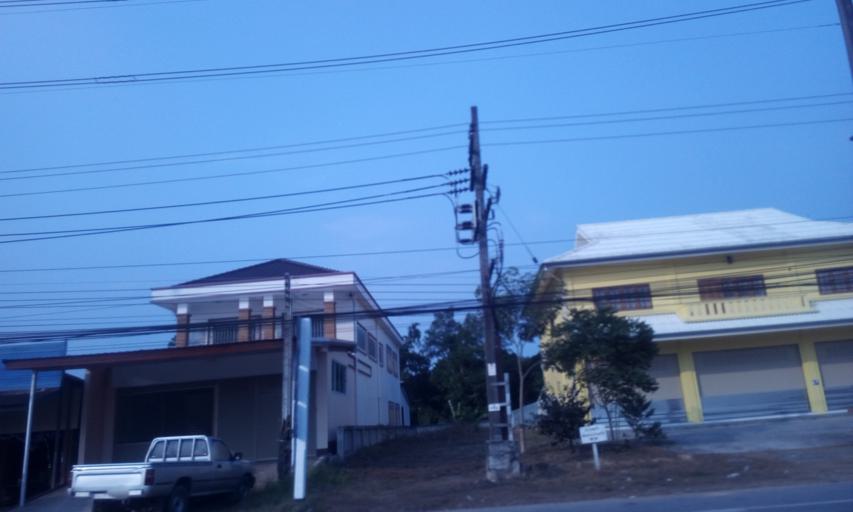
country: TH
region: Chanthaburi
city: Khlung
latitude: 12.4597
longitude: 102.2310
